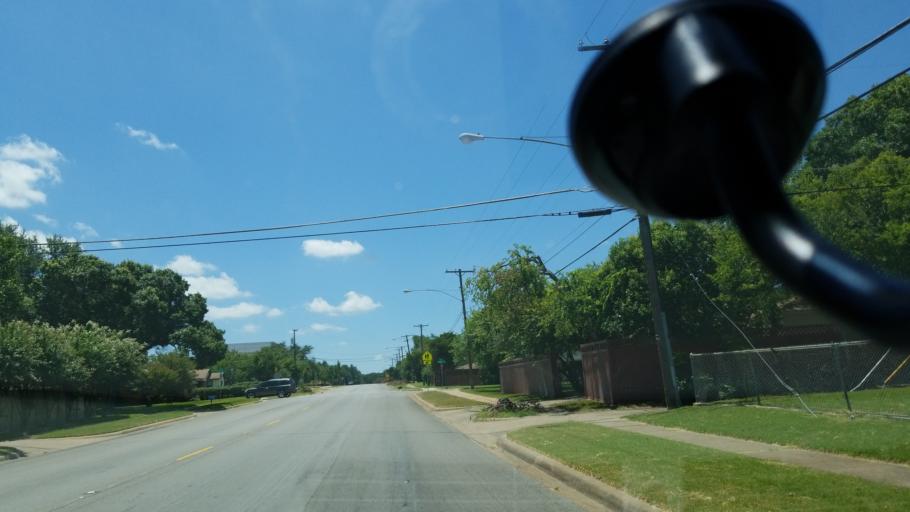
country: US
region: Texas
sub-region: Dallas County
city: Cockrell Hill
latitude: 32.6802
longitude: -96.8147
